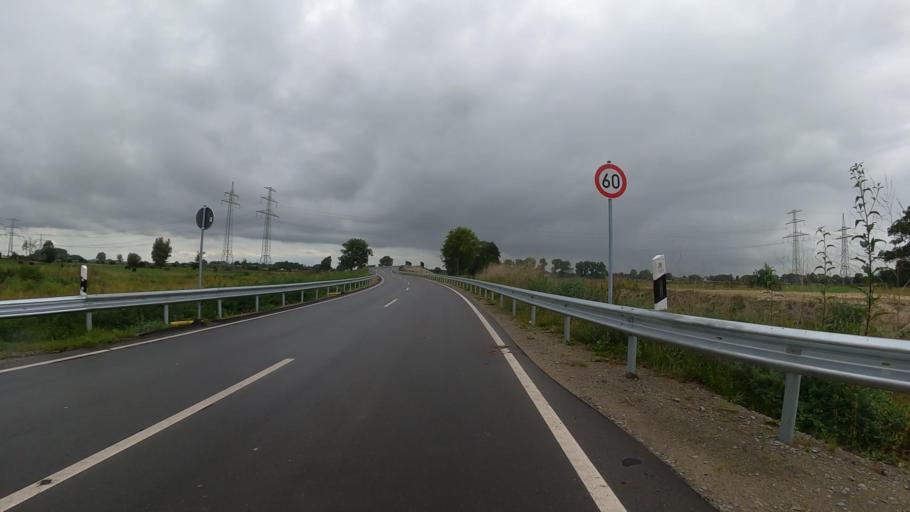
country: DE
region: Lower Saxony
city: Neu Wulmstorf
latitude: 53.4836
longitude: 9.7463
